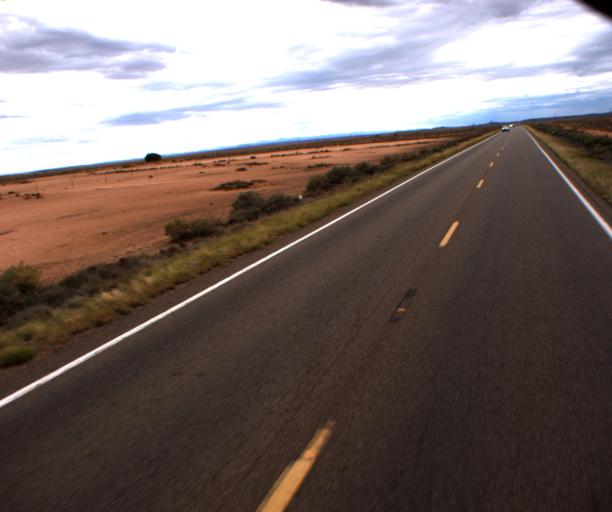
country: US
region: Arizona
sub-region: Navajo County
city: Holbrook
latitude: 34.8075
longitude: -110.1373
